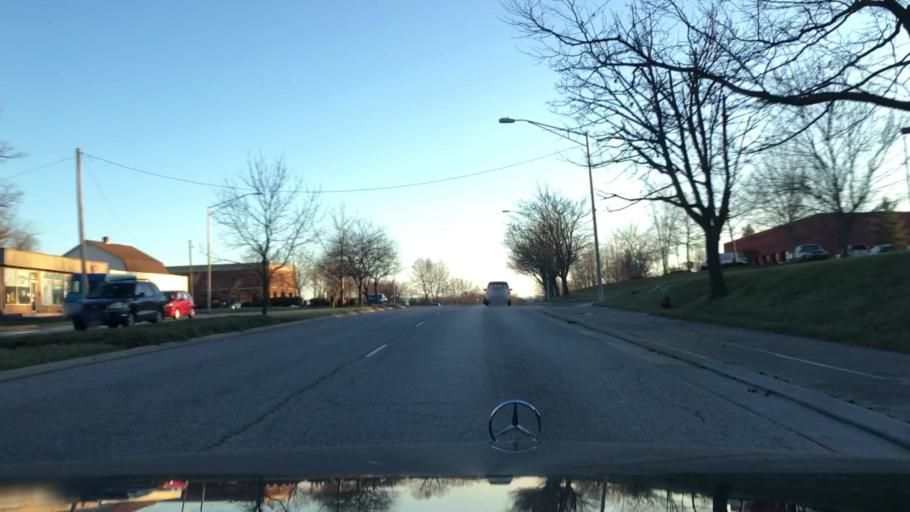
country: US
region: Virginia
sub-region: Montgomery County
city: Blacksburg
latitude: 37.2086
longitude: -80.3992
